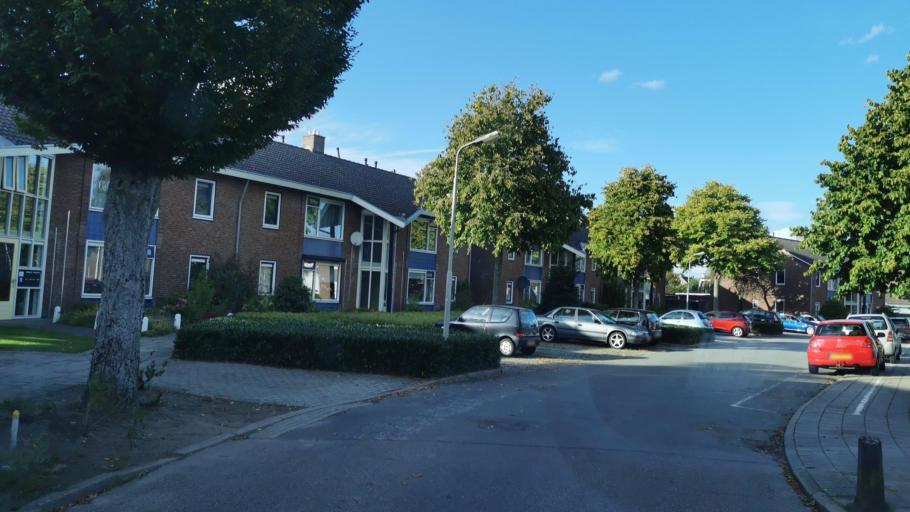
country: NL
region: Overijssel
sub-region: Gemeente Losser
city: Losser
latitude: 52.2638
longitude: 6.9999
